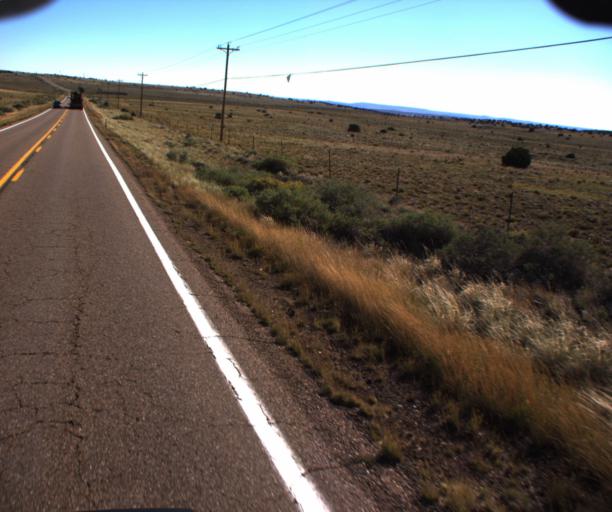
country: US
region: Arizona
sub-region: Apache County
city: Saint Johns
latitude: 34.4889
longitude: -109.5252
